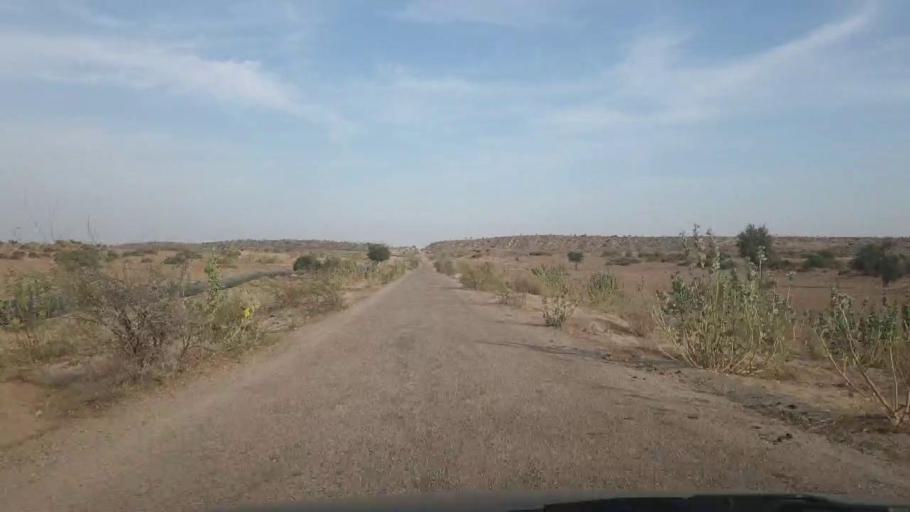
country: PK
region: Sindh
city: Nabisar
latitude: 25.0559
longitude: 69.6723
